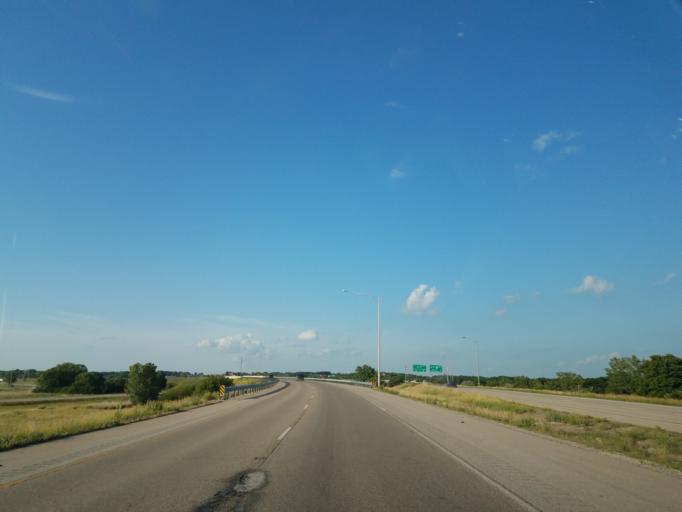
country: US
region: Illinois
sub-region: McLean County
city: Bloomington
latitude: 40.4368
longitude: -89.0259
